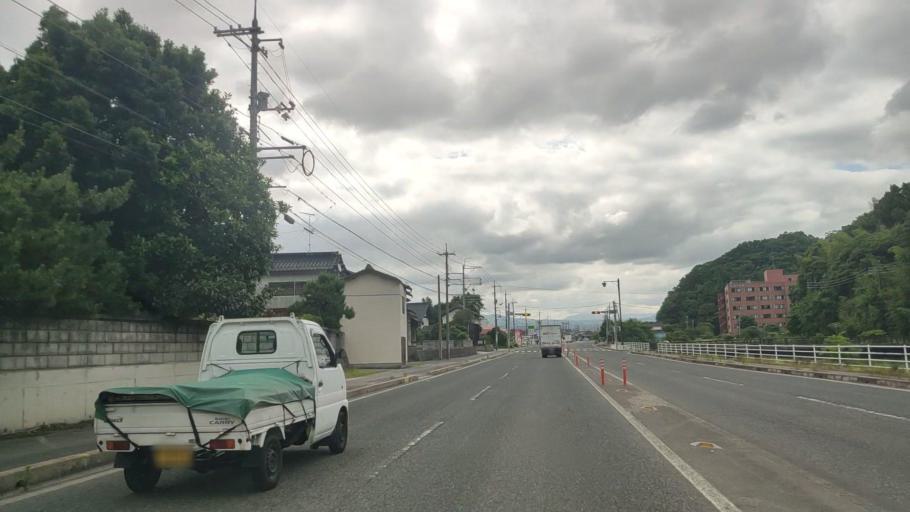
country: JP
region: Tottori
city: Yonago
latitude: 35.4126
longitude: 133.3555
